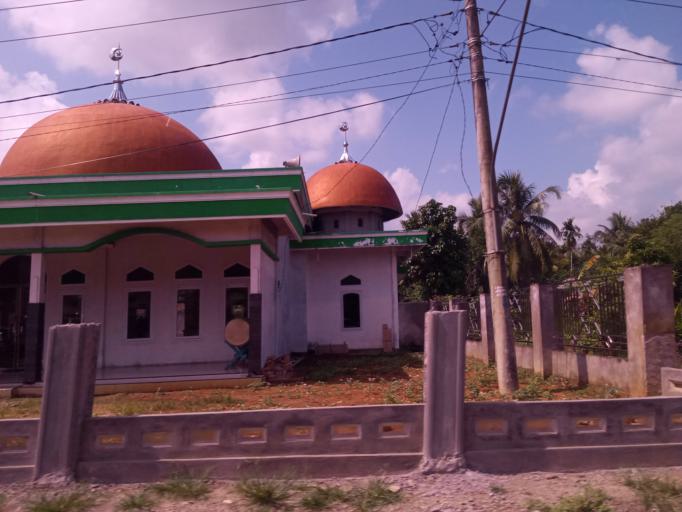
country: ID
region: Jambi
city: Muara Bulian
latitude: -1.7356
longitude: 103.1926
